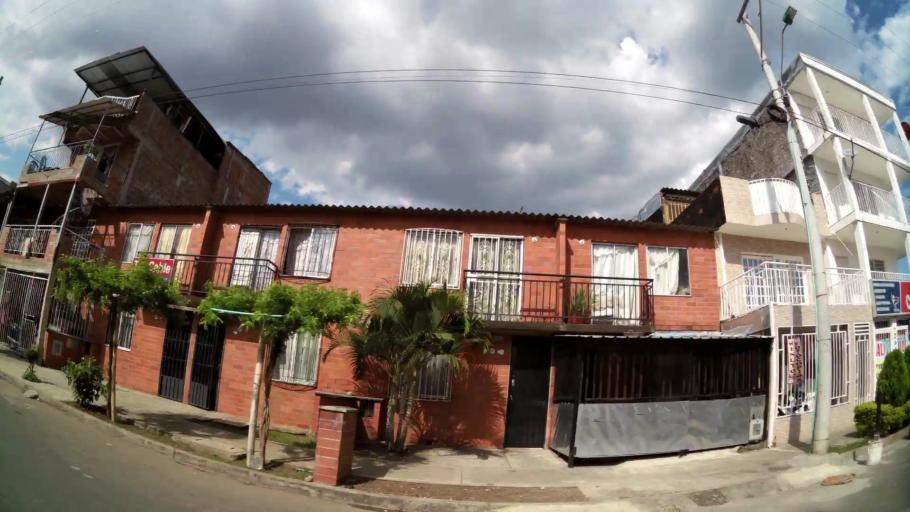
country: CO
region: Valle del Cauca
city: Cali
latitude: 3.3955
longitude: -76.5073
